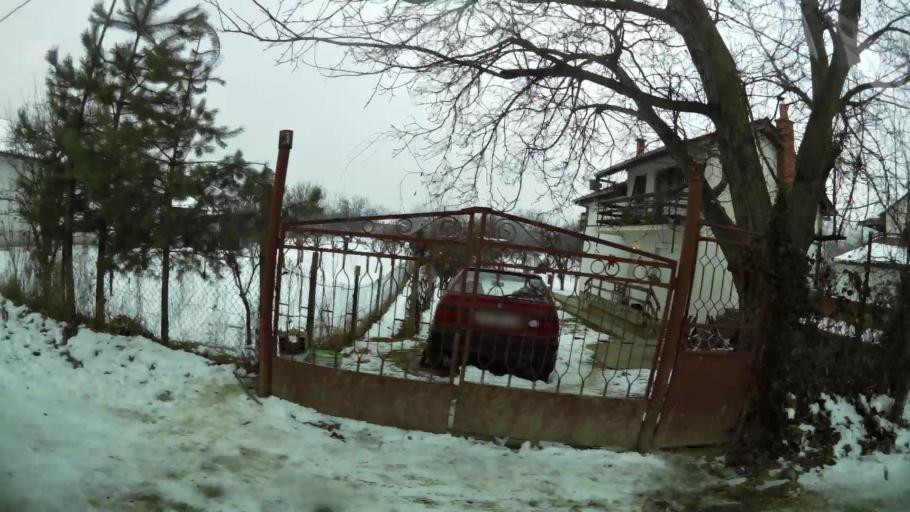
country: MK
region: Saraj
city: Saraj
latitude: 42.0390
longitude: 21.3588
